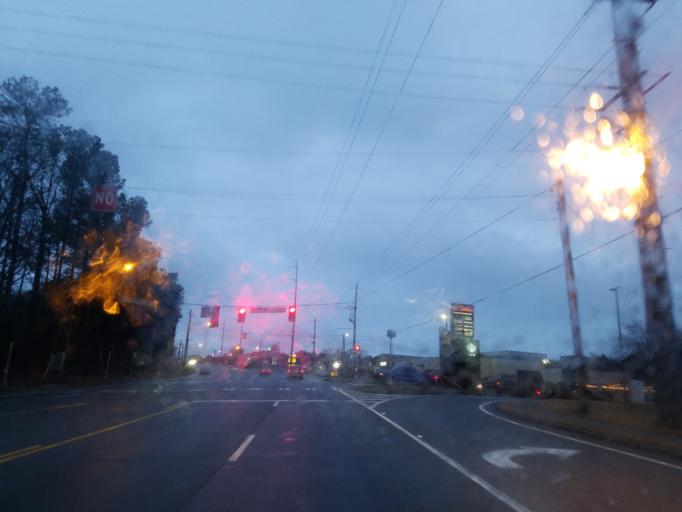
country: US
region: Georgia
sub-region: Fulton County
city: Roswell
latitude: 34.0173
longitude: -84.3114
